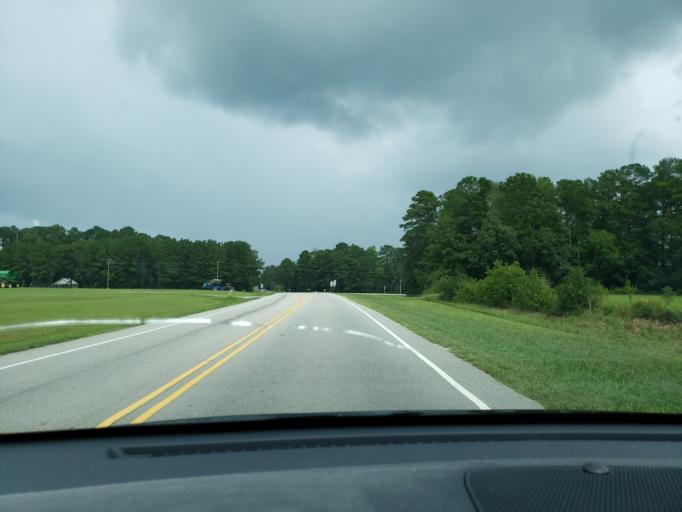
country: US
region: North Carolina
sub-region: Bladen County
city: Bladenboro
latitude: 34.5009
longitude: -78.6558
